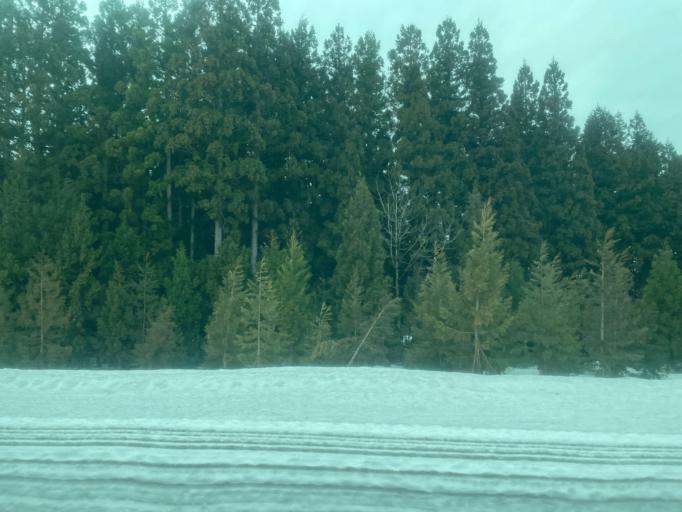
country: JP
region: Niigata
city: Shiozawa
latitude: 36.9149
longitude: 138.8487
